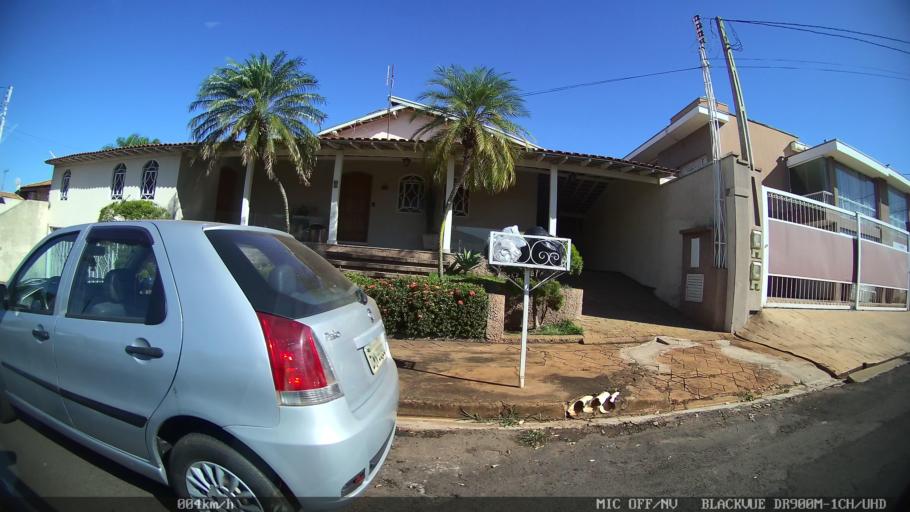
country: BR
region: Sao Paulo
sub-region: Olimpia
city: Olimpia
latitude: -20.7310
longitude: -48.9156
